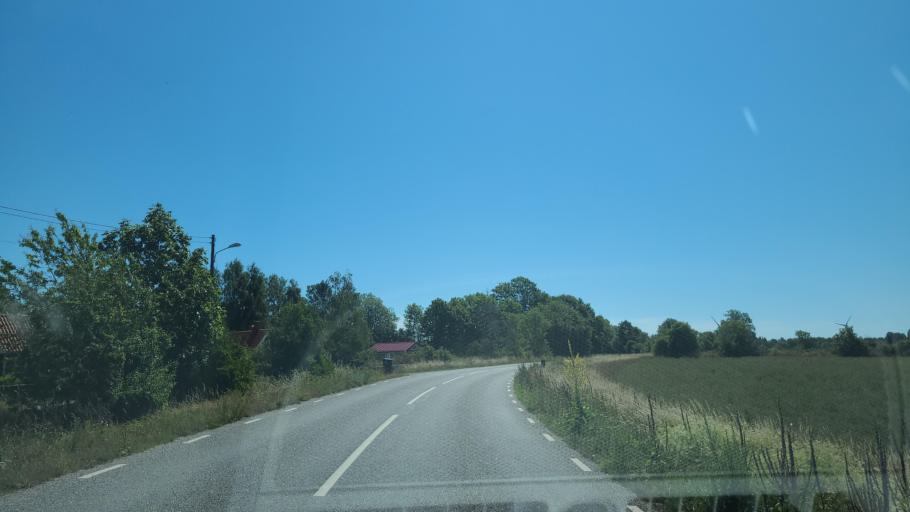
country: SE
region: Kalmar
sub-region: Borgholms Kommun
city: Borgholm
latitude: 56.7713
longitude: 16.5829
